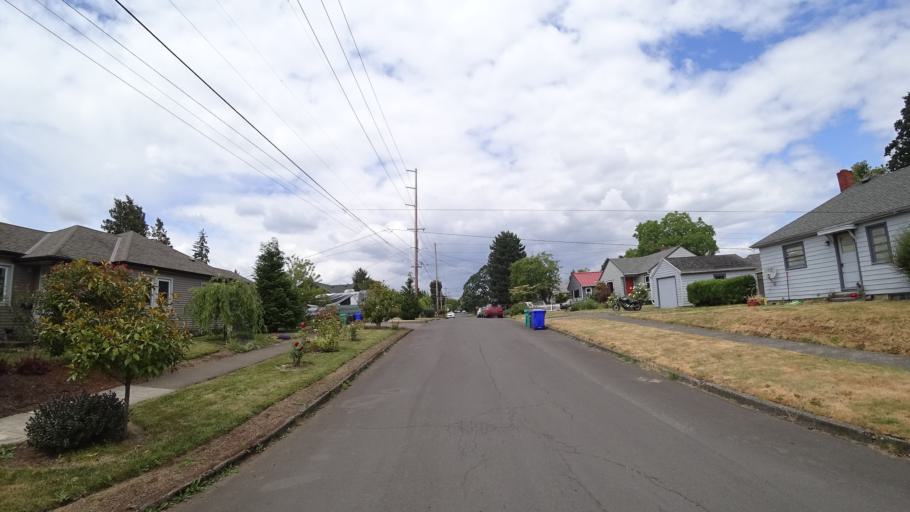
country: US
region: Oregon
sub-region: Washington County
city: West Haven
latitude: 45.5833
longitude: -122.7290
